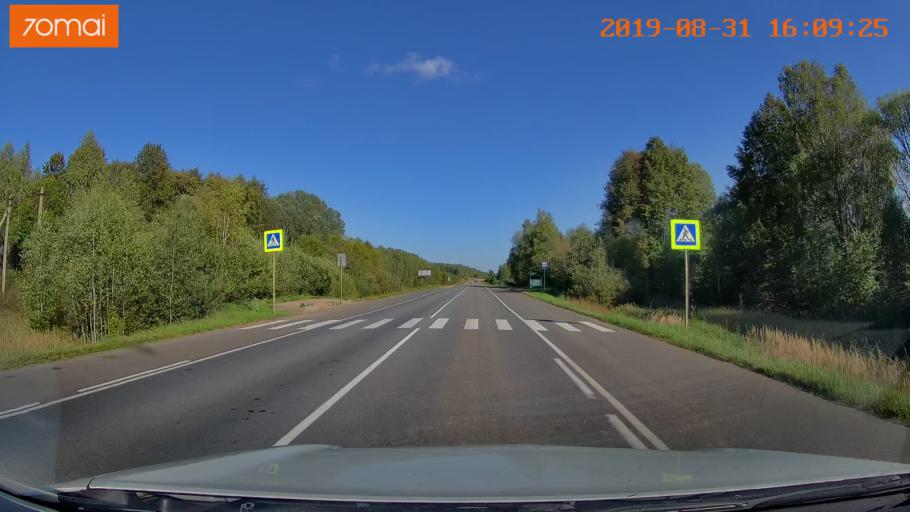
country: RU
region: Kaluga
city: Yukhnov
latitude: 54.5885
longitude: 35.3985
